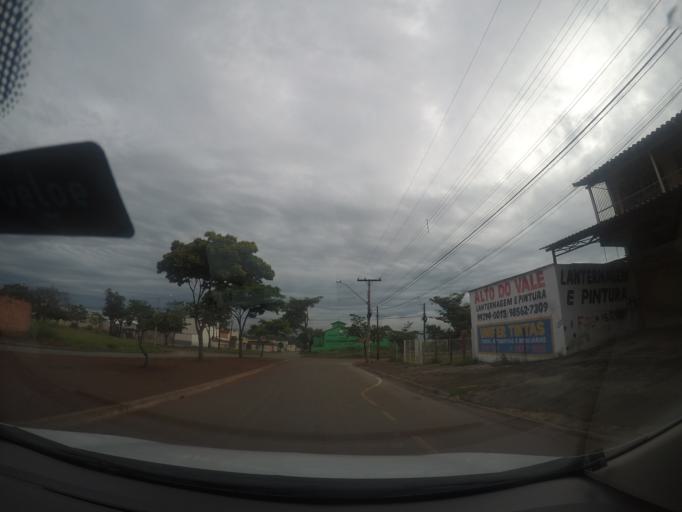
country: BR
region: Goias
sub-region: Goiania
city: Goiania
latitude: -16.6055
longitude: -49.3124
